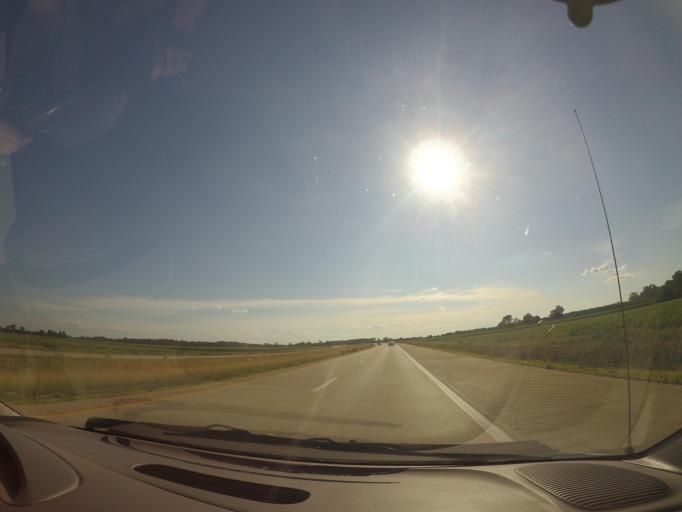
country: US
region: Ohio
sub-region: Lucas County
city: Whitehouse
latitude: 41.4337
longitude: -83.8764
